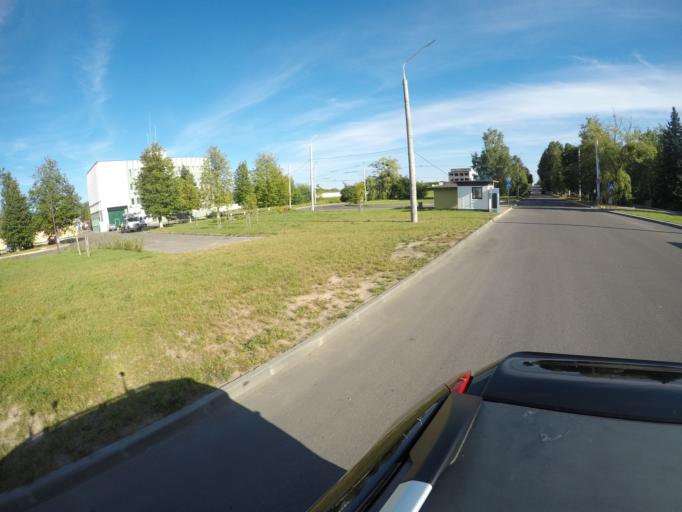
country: BY
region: Grodnenskaya
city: Hrodna
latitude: 53.7146
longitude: 23.8253
